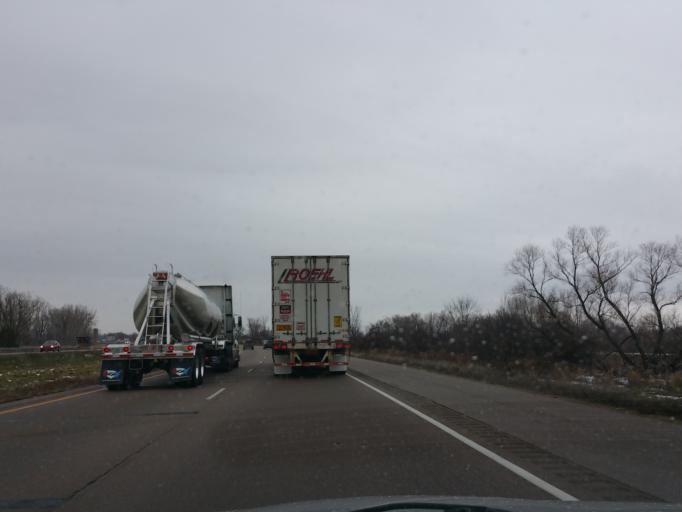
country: US
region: Wisconsin
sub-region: Rock County
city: Edgerton
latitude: 42.9100
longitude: -89.0854
